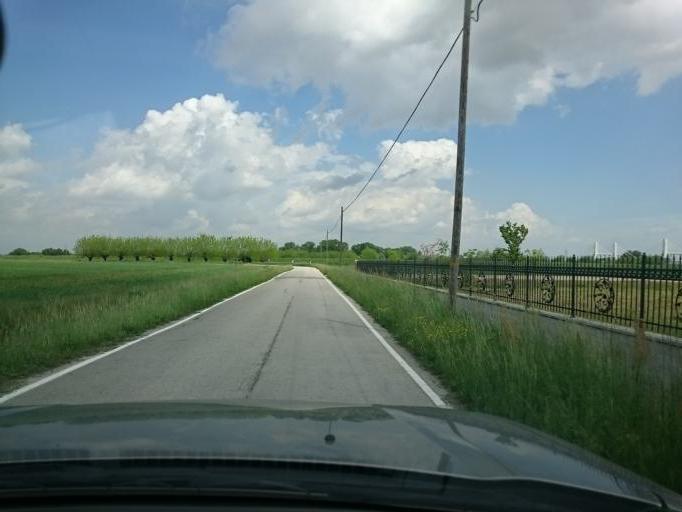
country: IT
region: Veneto
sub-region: Provincia di Vicenza
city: Villaganzerla
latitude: 45.4590
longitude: 11.6219
